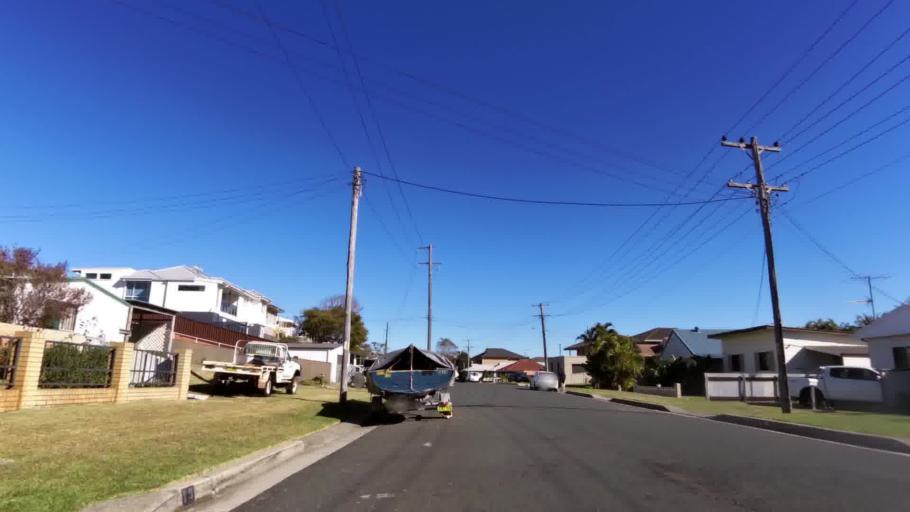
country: AU
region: New South Wales
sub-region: Wollongong
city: Lake Heights
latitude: -34.4988
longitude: 150.8864
